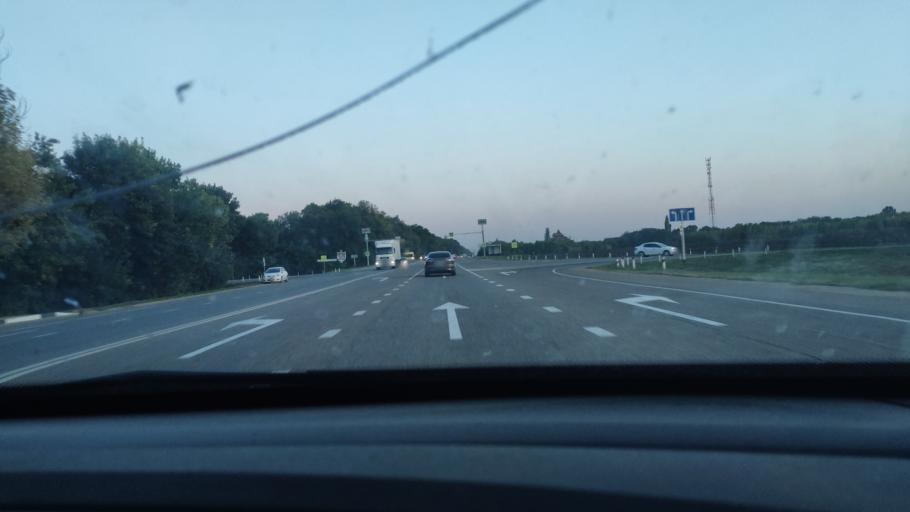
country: RU
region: Krasnodarskiy
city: Medvedovskaya
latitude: 45.4542
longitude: 38.9894
